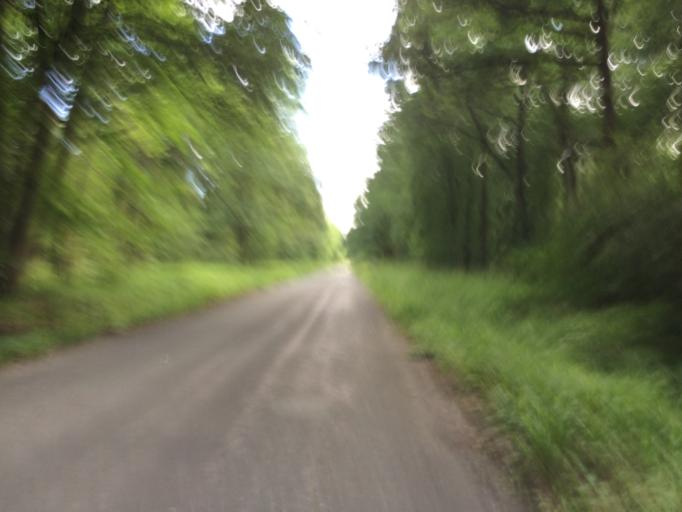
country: FR
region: Ile-de-France
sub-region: Departement de l'Essonne
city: Brunoy
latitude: 48.6662
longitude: 2.4850
